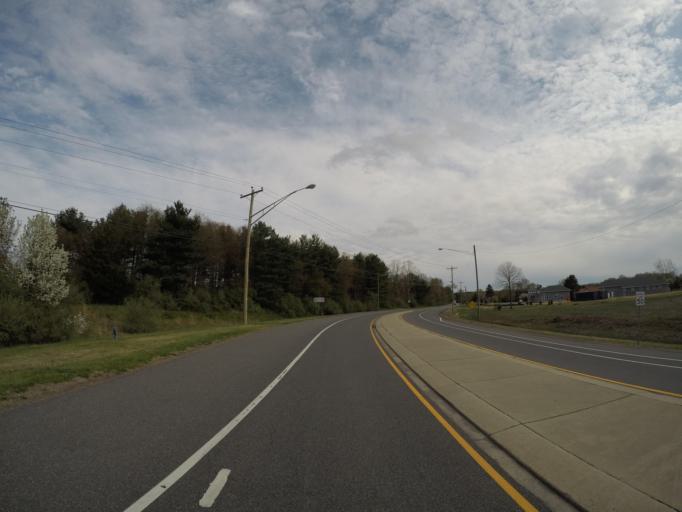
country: US
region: Delaware
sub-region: New Castle County
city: Glasgow
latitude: 39.5577
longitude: -75.7366
